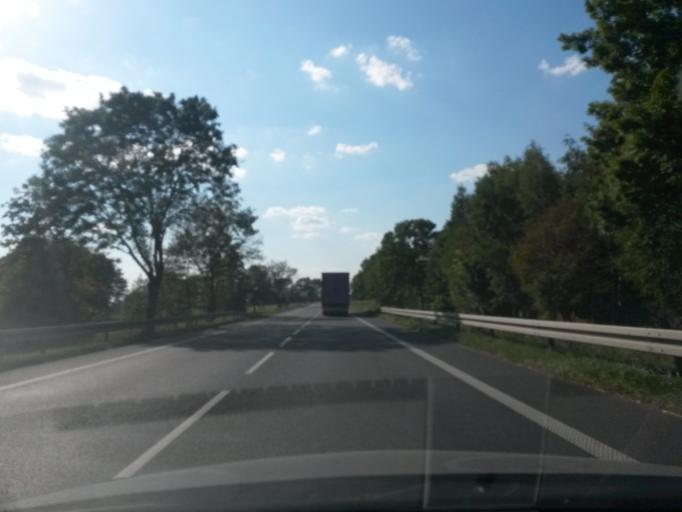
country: PL
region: Masovian Voivodeship
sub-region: Powiat sierpecki
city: Zawidz
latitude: 52.8095
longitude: 19.8249
